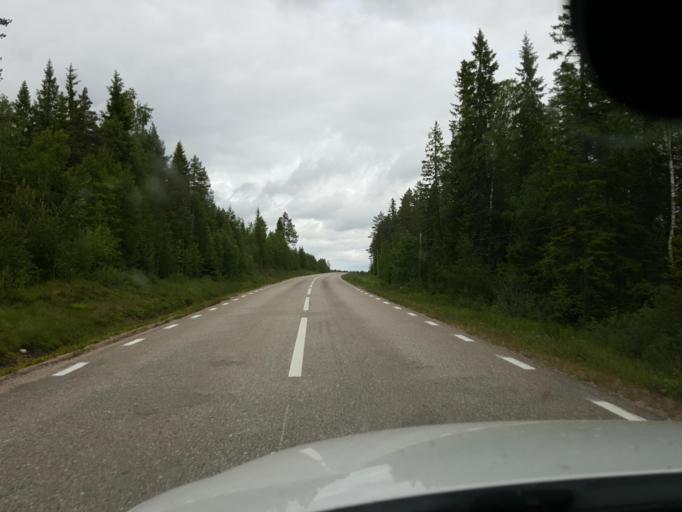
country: SE
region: Gaevleborg
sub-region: Ljusdals Kommun
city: Farila
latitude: 61.7580
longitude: 15.4763
